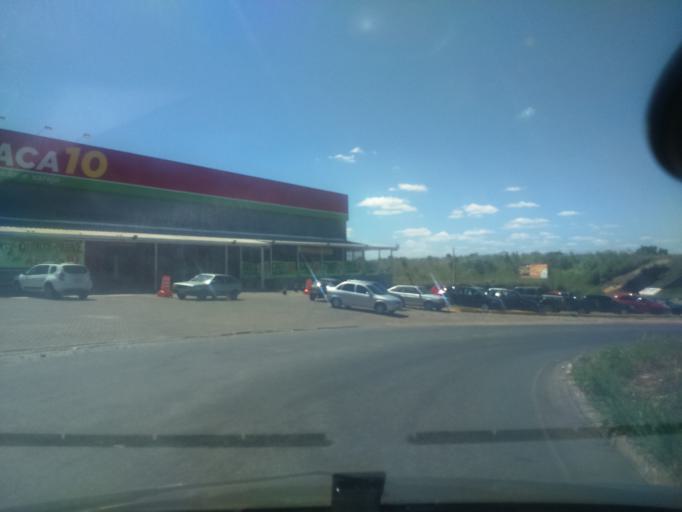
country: BR
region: Goias
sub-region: Luziania
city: Luziania
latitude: -16.1115
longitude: -47.9701
